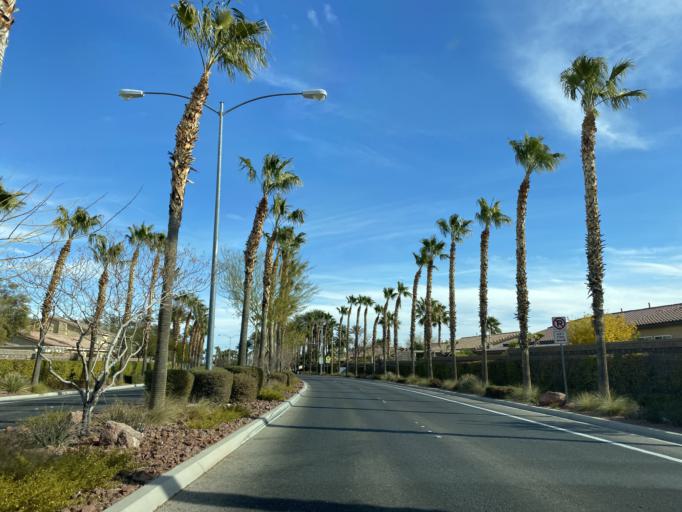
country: US
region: Nevada
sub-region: Clark County
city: Enterprise
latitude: 36.0480
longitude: -115.2502
